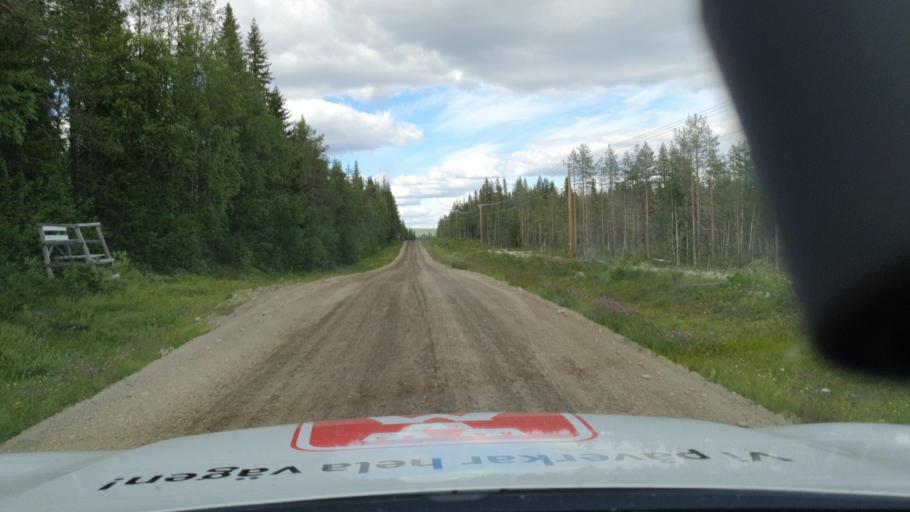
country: SE
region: Vaesterbotten
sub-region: Lycksele Kommun
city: Lycksele
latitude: 64.3120
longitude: 18.2998
